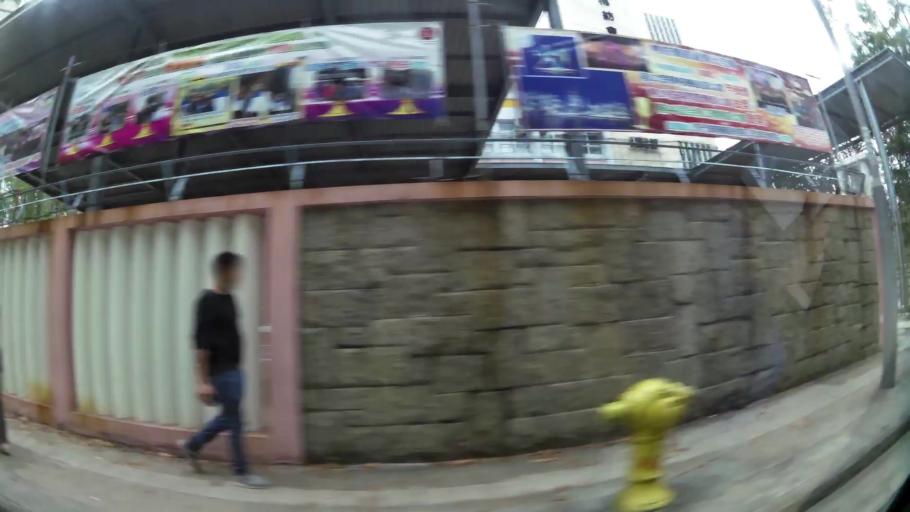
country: HK
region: Tsuen Wan
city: Tsuen Wan
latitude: 22.3629
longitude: 114.1294
